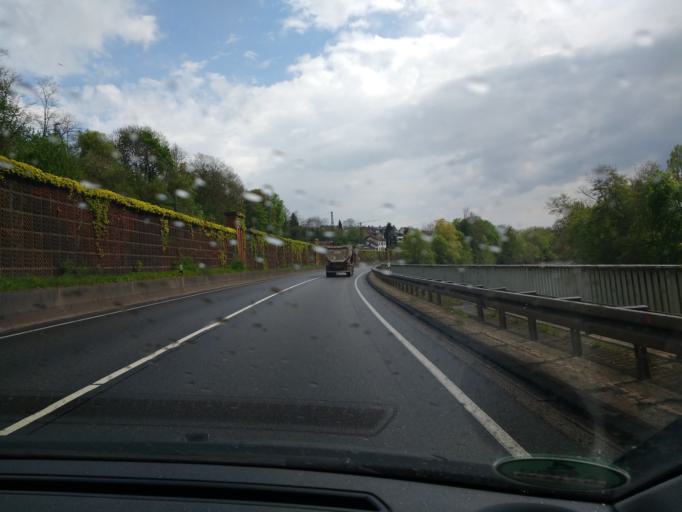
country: DE
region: Saarland
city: Kleinblittersdorf
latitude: 49.1651
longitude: 7.0327
